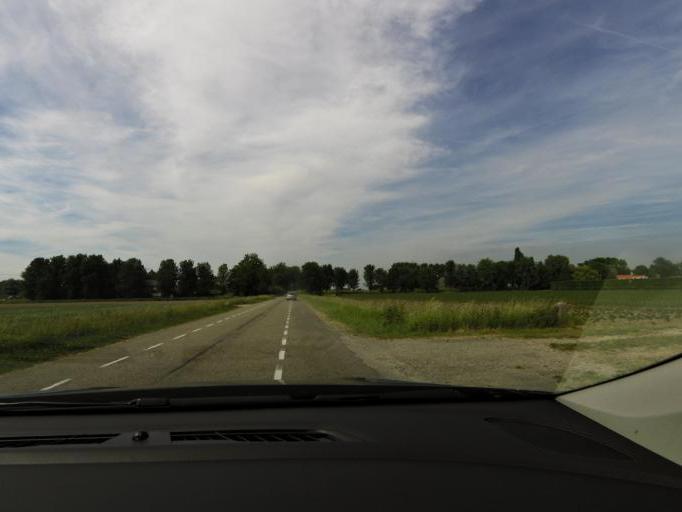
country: NL
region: North Brabant
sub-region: Gemeente Moerdijk
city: Willemstad
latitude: 51.7406
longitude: 4.4140
